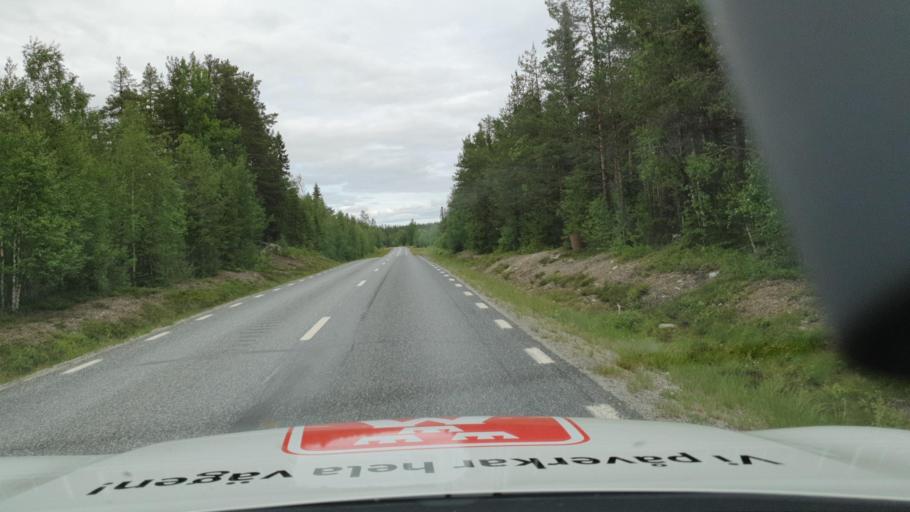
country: SE
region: Vaesterbotten
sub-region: Asele Kommun
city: Insjon
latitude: 64.2491
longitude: 17.5490
